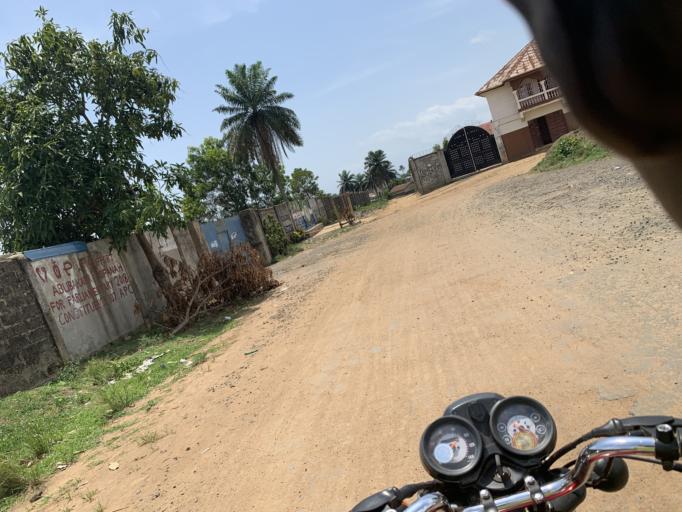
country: SL
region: Western Area
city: Waterloo
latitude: 8.3405
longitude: -13.0329
